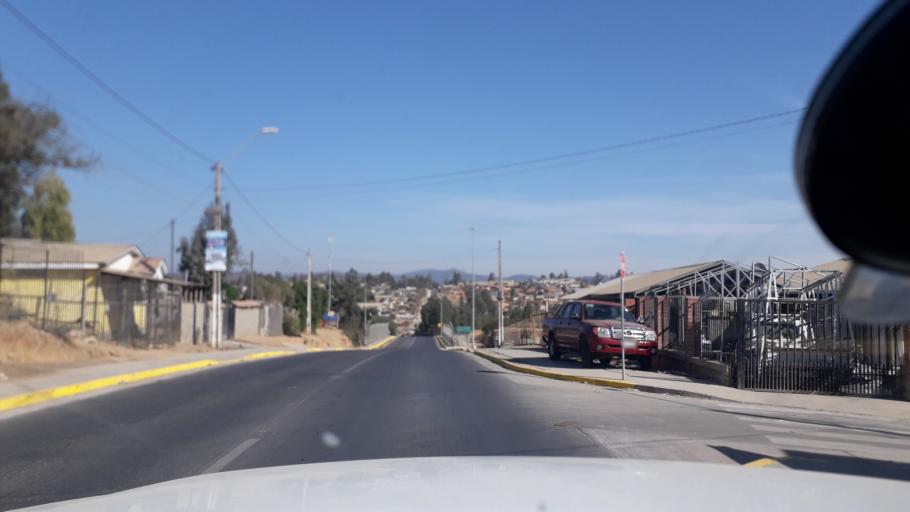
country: CL
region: Valparaiso
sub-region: Provincia de Marga Marga
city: Villa Alemana
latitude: -33.0647
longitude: -71.4029
